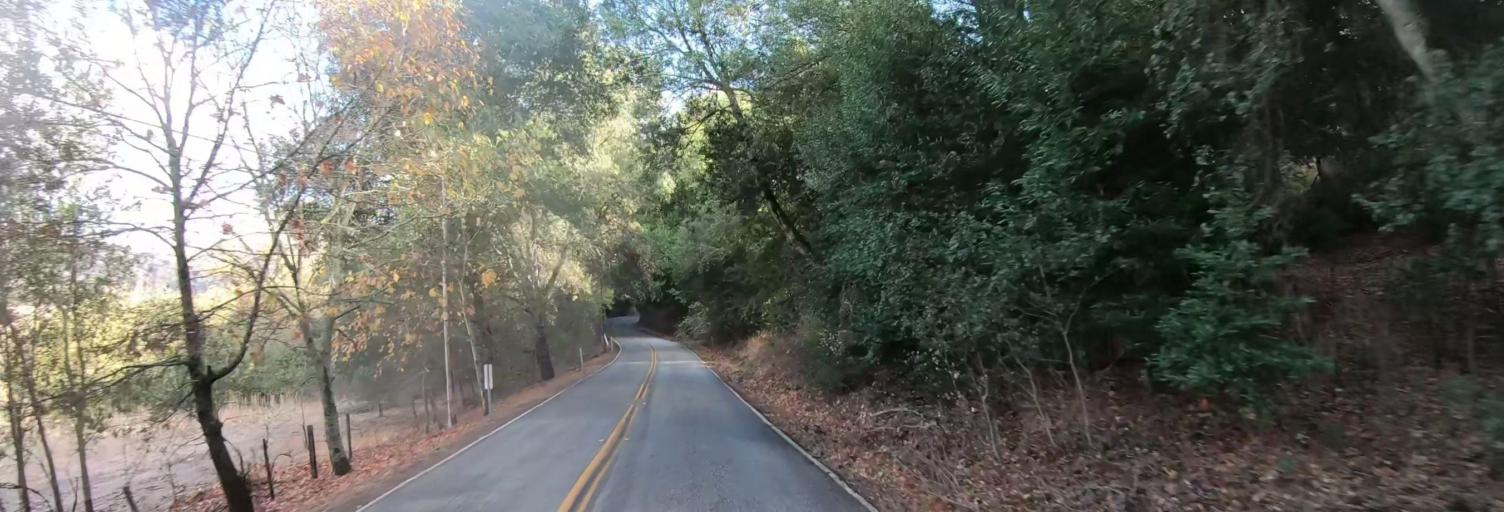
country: US
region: California
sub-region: Santa Clara County
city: East Foothills
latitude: 37.3494
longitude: -121.7310
